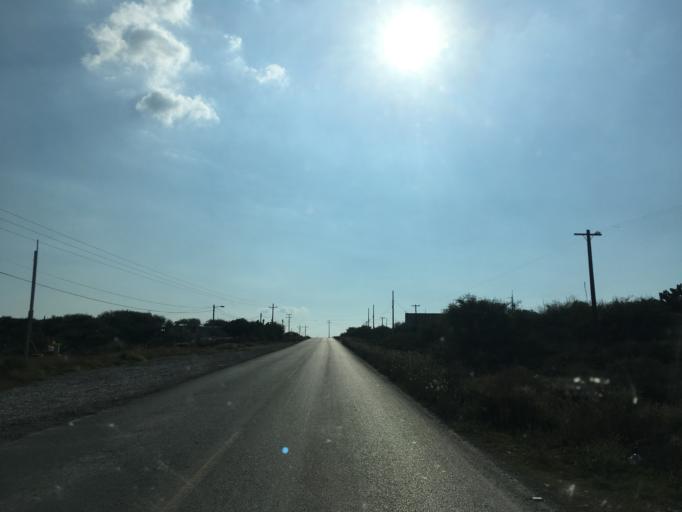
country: MX
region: Hidalgo
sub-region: Ixmiquilpan
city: El Nith
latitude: 20.5760
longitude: -99.1391
